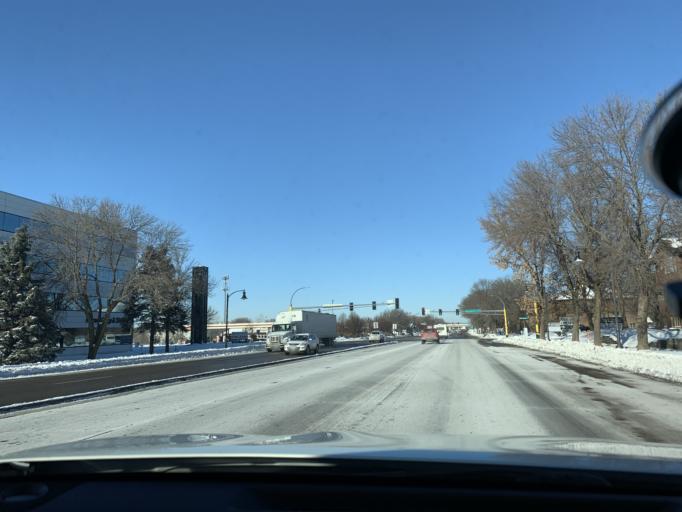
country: US
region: Minnesota
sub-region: Anoka County
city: Coon Rapids
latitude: 45.1374
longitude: -93.2723
